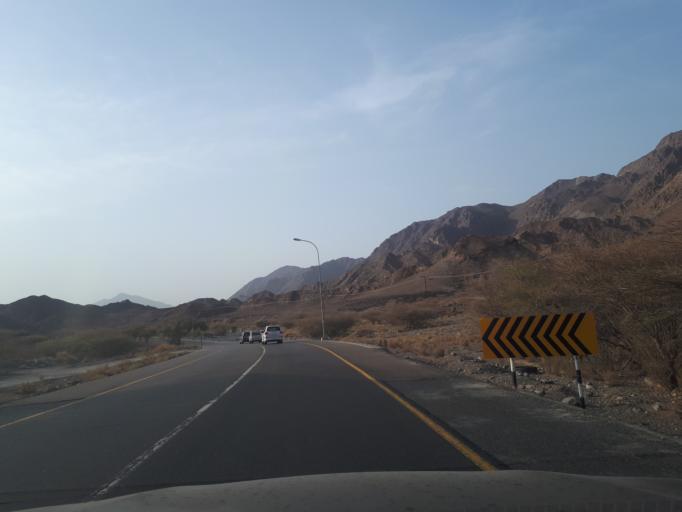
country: OM
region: Muhafazat ad Dakhiliyah
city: Sufalat Sama'il
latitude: 23.1674
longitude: 58.1027
